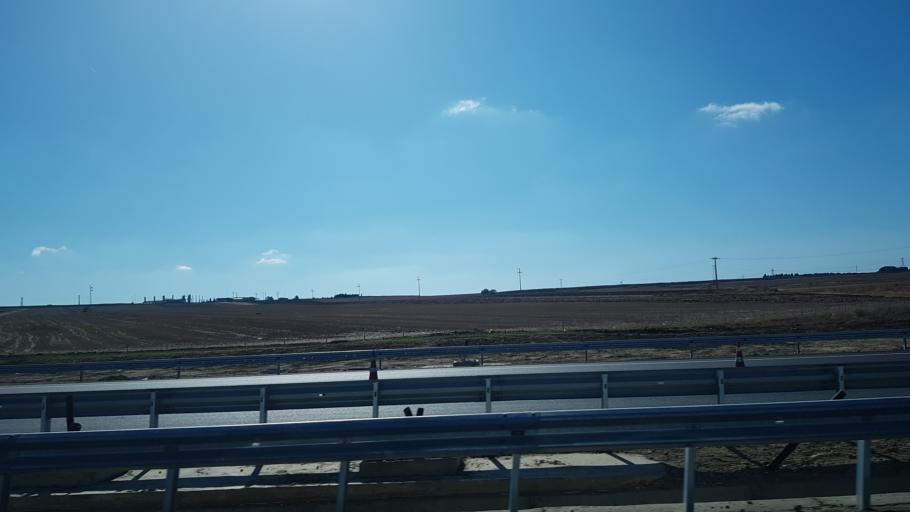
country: TR
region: Istanbul
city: Silivri
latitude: 41.1125
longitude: 28.1684
